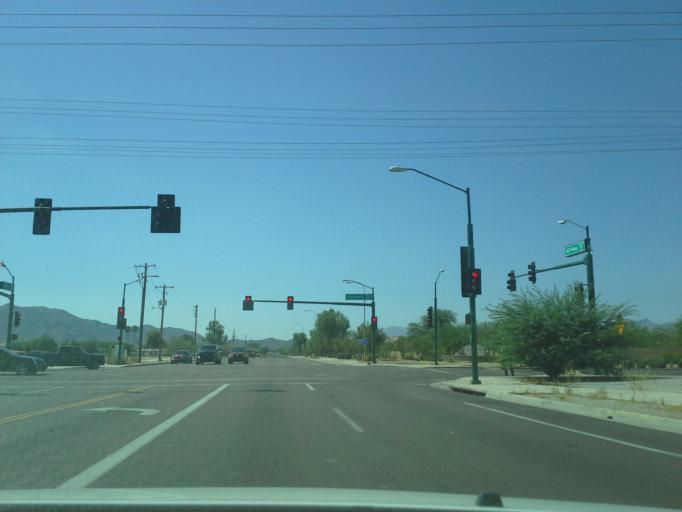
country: US
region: Arizona
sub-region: Maricopa County
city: Laveen
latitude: 33.3925
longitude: -112.1509
